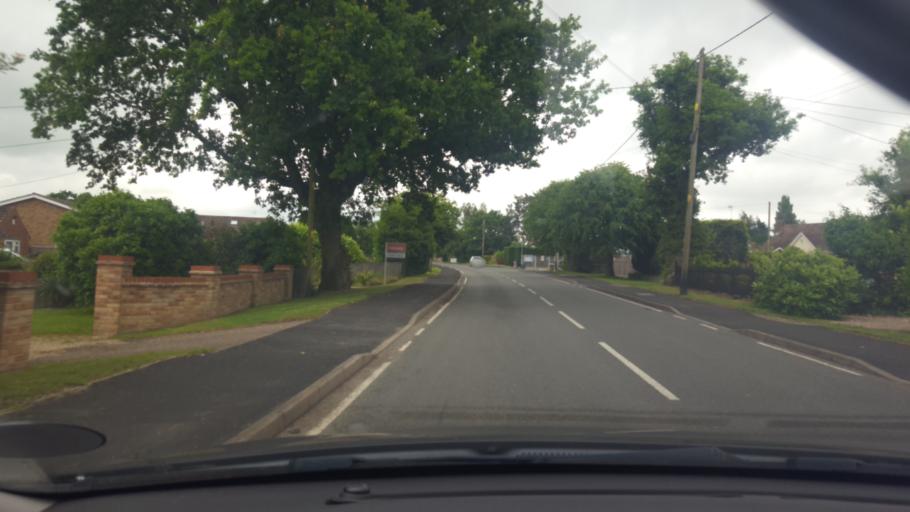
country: GB
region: England
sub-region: Essex
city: Saint Osyth
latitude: 51.7941
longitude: 1.0531
